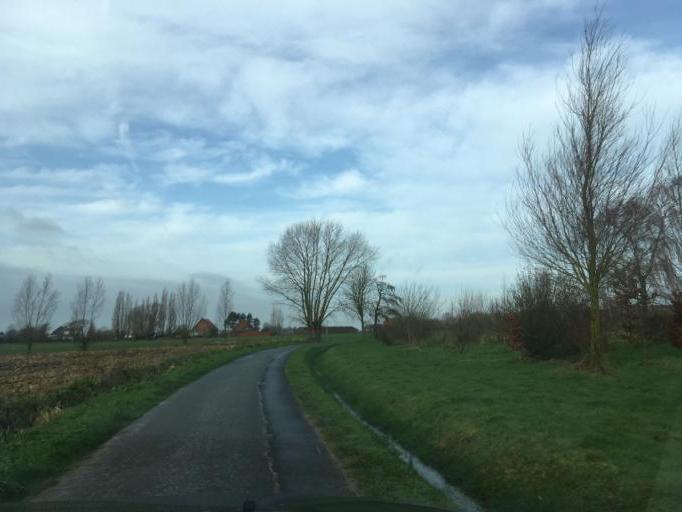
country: BE
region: Flanders
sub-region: Provincie West-Vlaanderen
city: Hooglede
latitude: 50.9650
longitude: 3.0834
